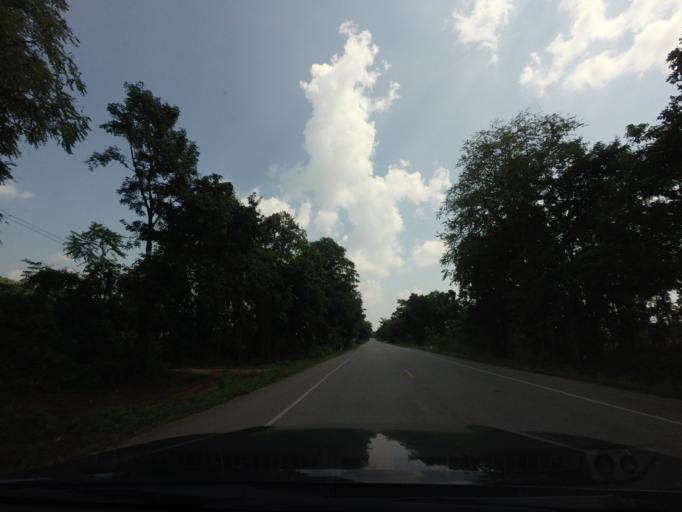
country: TH
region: Phitsanulok
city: Chat Trakan
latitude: 17.2730
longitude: 100.5432
